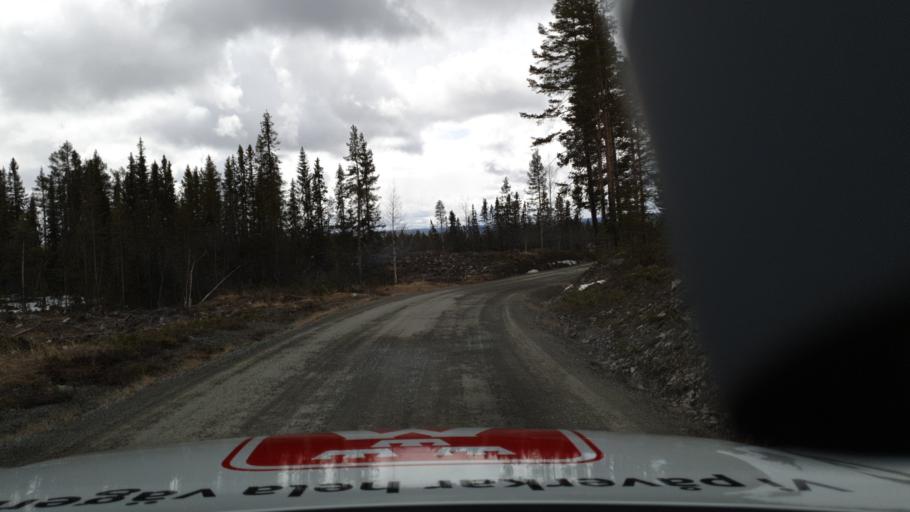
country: SE
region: Jaemtland
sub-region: Are Kommun
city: Jarpen
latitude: 62.8108
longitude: 13.8087
